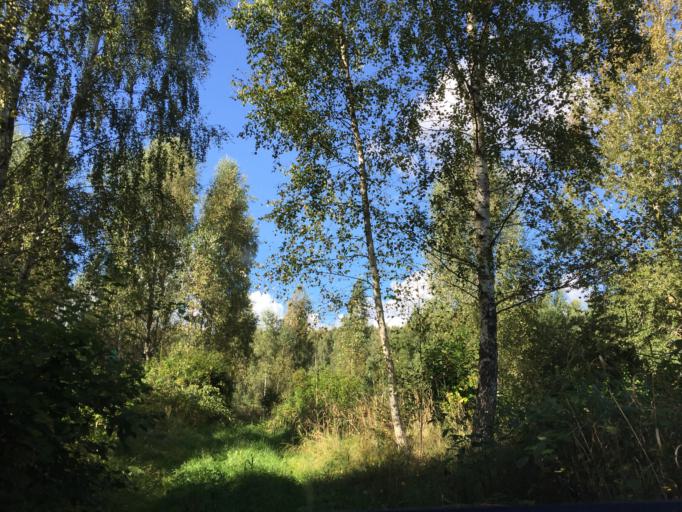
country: LV
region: Kuldigas Rajons
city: Kuldiga
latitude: 56.9969
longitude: 21.8206
